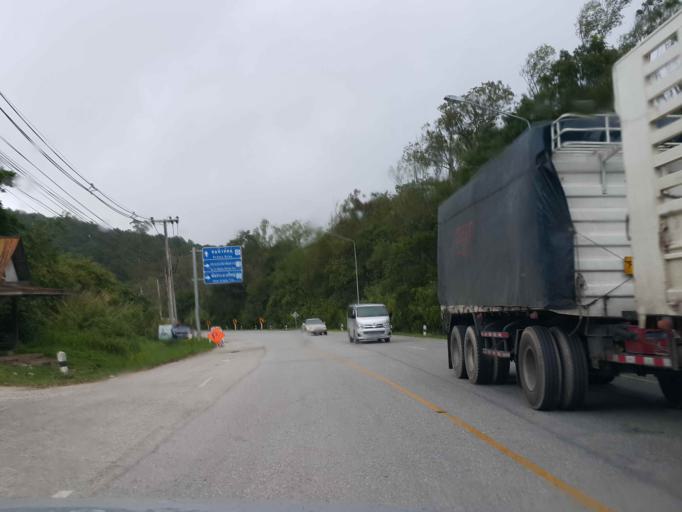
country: TH
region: Tak
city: Tak
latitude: 16.7681
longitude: 98.9304
